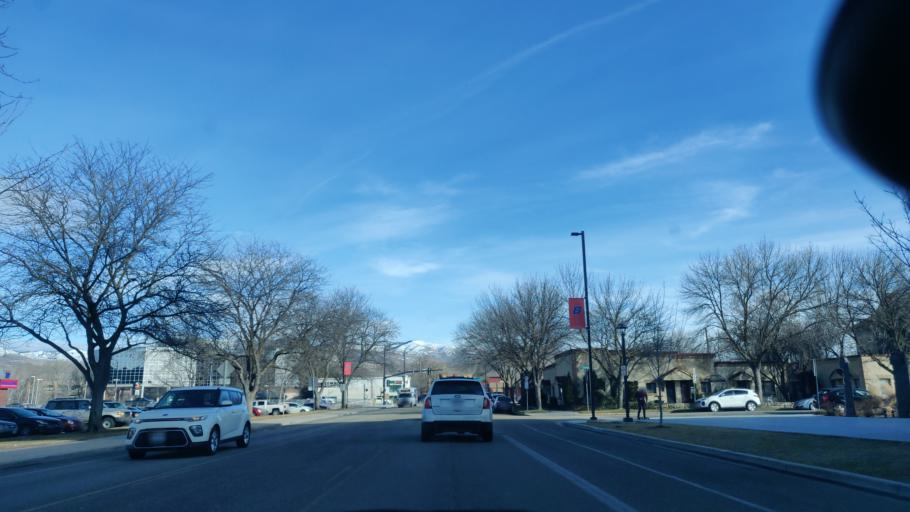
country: US
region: Idaho
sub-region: Ada County
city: Boise
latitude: 43.6010
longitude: -116.1955
